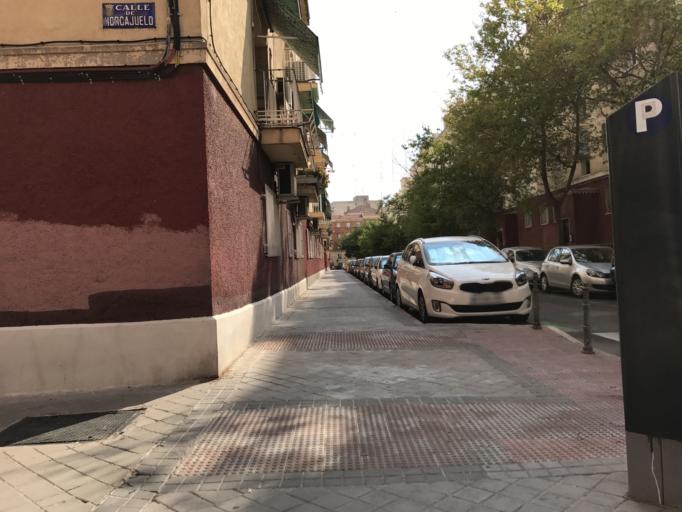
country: ES
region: Madrid
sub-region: Provincia de Madrid
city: Salamanca
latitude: 40.4401
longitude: -3.6776
